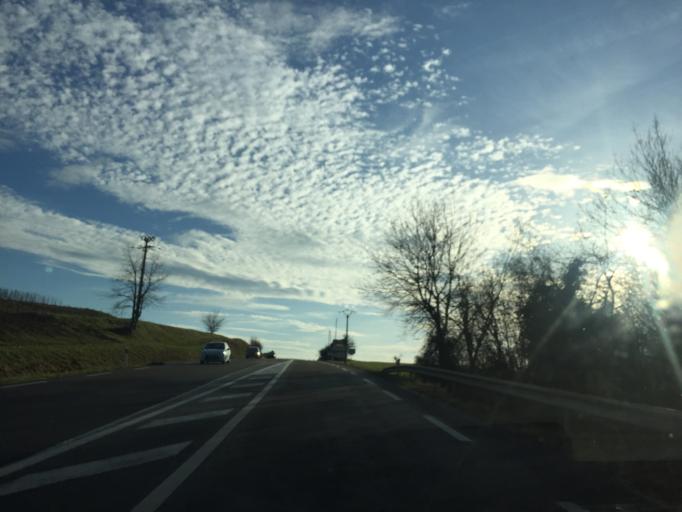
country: FR
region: Franche-Comte
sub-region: Departement du Jura
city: Arbois
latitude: 46.9329
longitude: 5.7761
